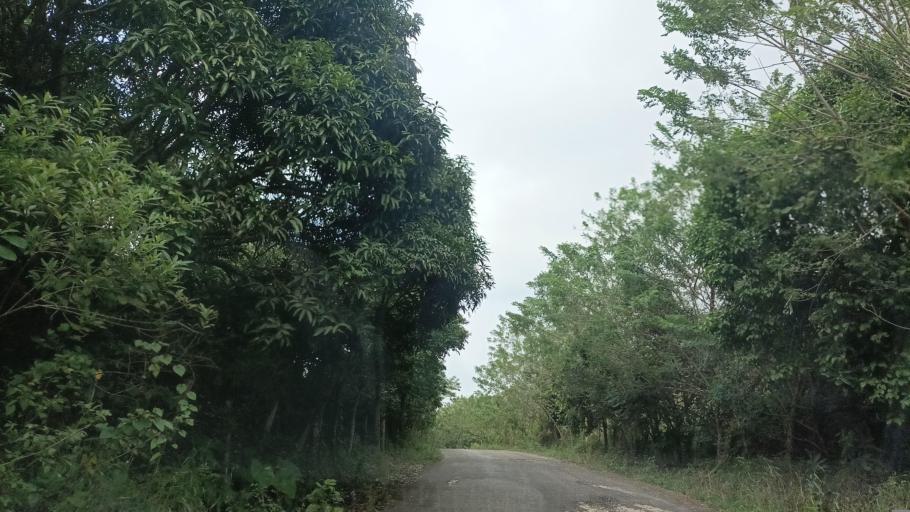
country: MX
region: Veracruz
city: Allende
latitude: 18.0996
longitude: -94.2938
